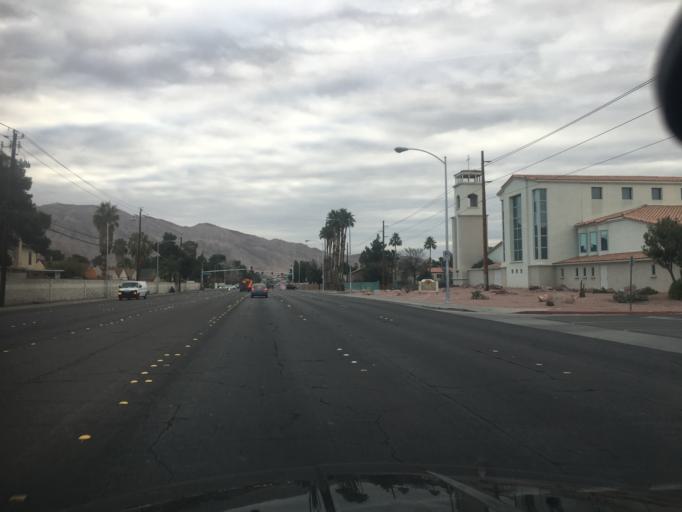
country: US
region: Nevada
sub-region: Clark County
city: Sunrise Manor
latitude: 36.1593
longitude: -115.0557
